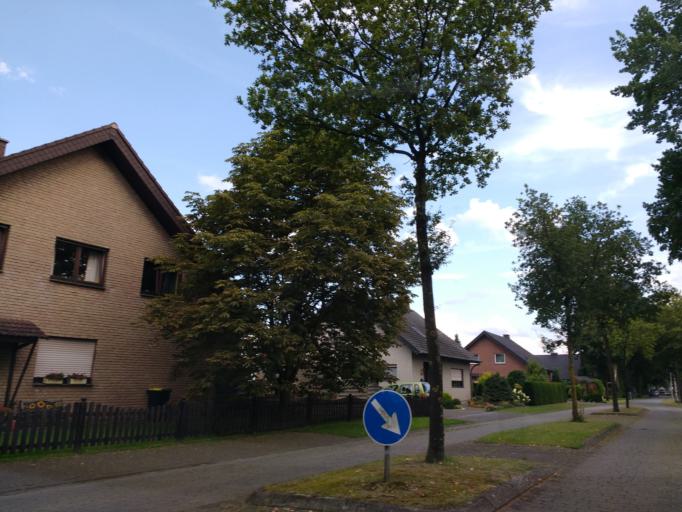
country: DE
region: North Rhine-Westphalia
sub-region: Regierungsbezirk Detmold
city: Delbruck
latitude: 51.7991
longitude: 8.5494
